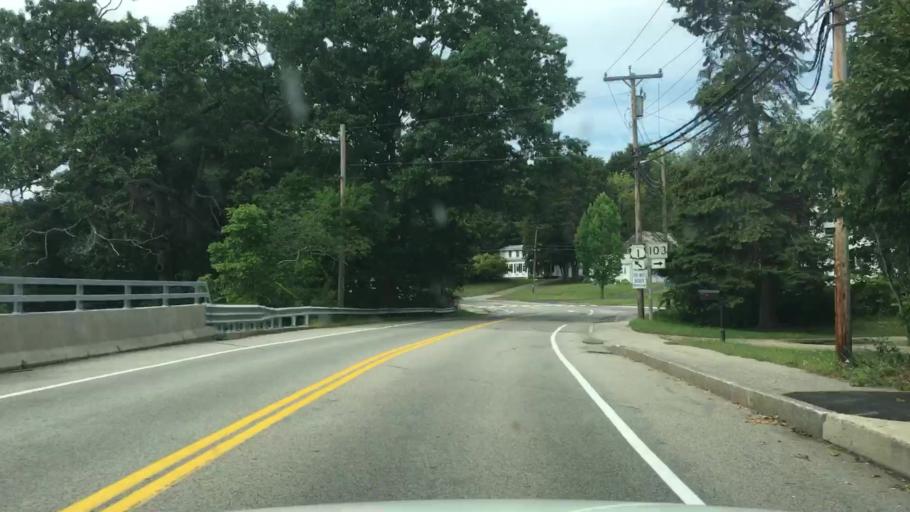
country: US
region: Maine
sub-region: York County
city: Kittery
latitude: 43.0885
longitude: -70.7540
